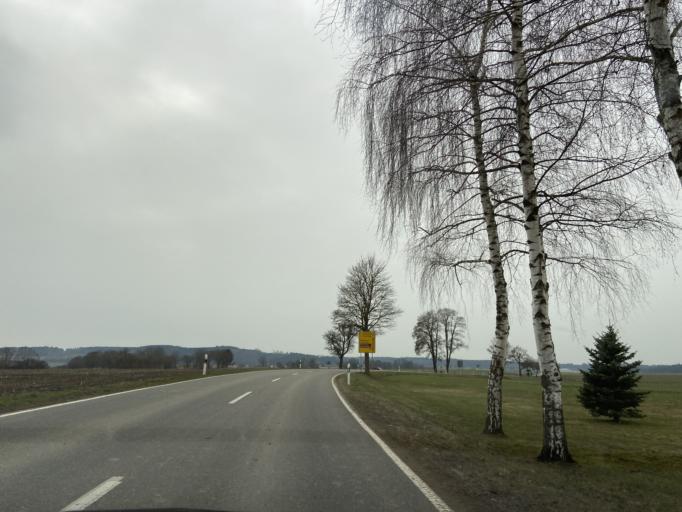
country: DE
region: Baden-Wuerttemberg
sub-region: Tuebingen Region
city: Ostrach
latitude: 47.9287
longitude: 9.3546
